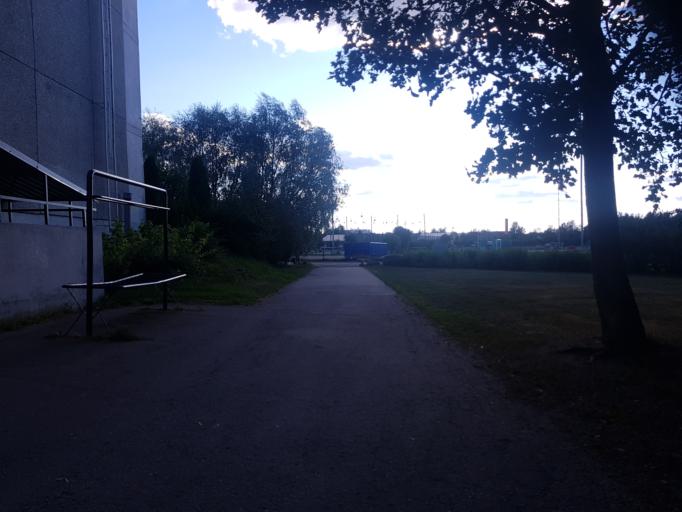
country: FI
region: Uusimaa
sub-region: Helsinki
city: Vantaa
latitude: 60.2736
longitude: 24.9846
